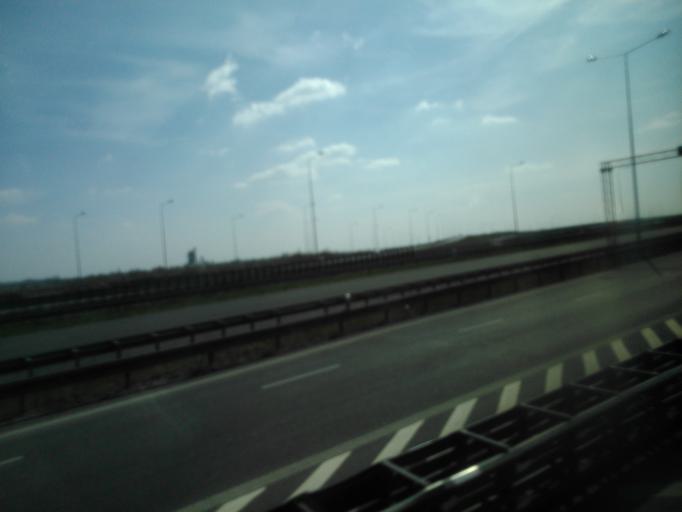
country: PL
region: Lodz Voivodeship
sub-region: Powiat zgierski
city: Strykow
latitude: 51.8949
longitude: 19.6319
